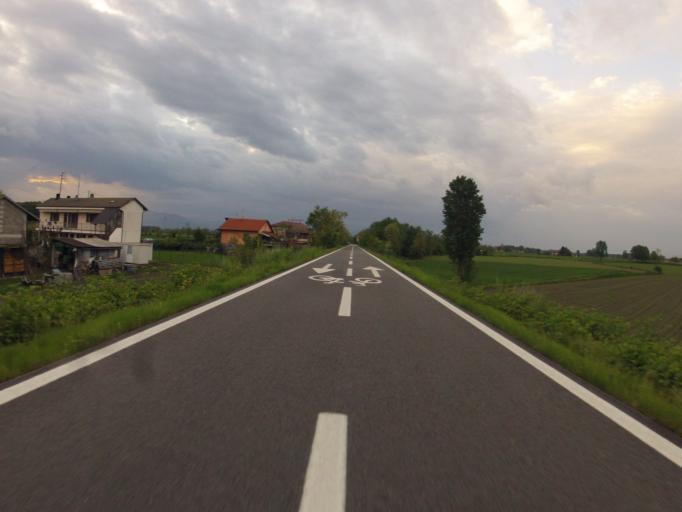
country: IT
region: Piedmont
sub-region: Provincia di Torino
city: Vigone
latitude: 44.8145
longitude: 7.4985
